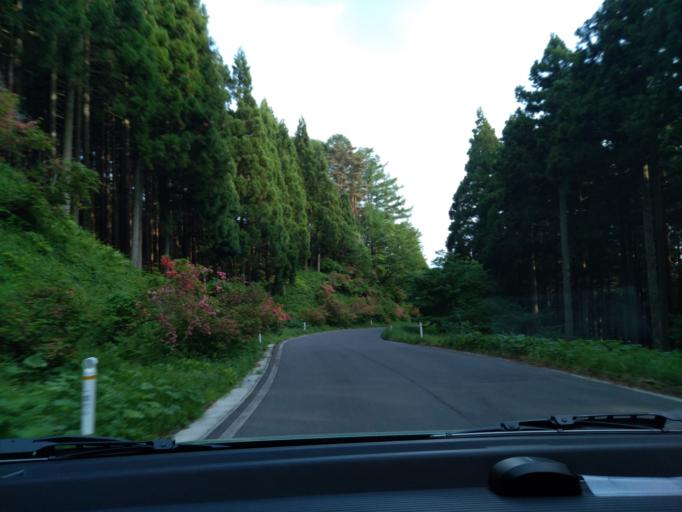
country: JP
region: Iwate
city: Ofunato
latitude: 38.9619
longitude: 141.4489
